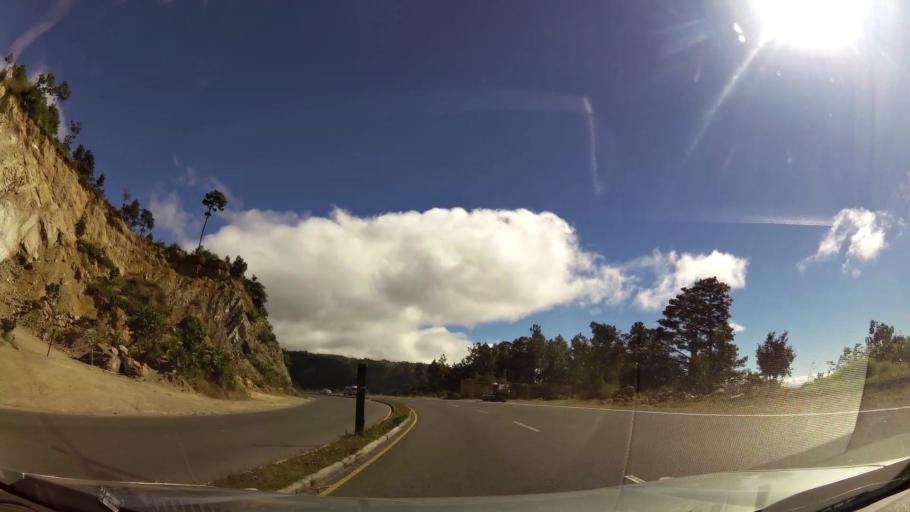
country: GT
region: Solola
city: Solola
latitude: 14.8274
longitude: -91.1848
